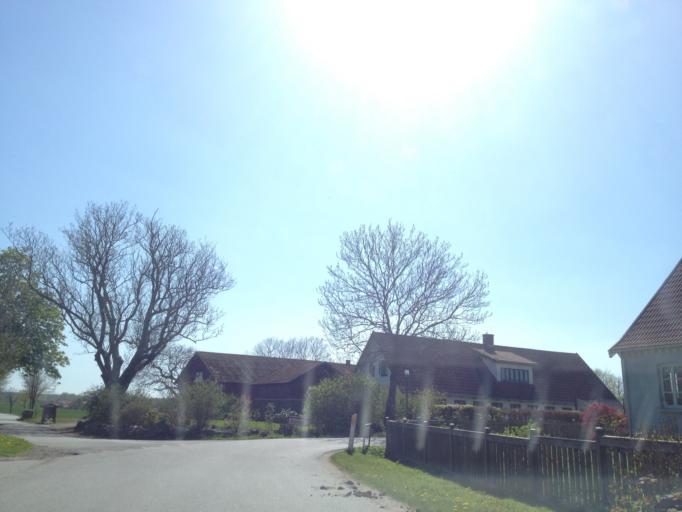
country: DK
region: Zealand
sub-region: Koge Kommune
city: Borup
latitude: 55.5094
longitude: 11.9897
